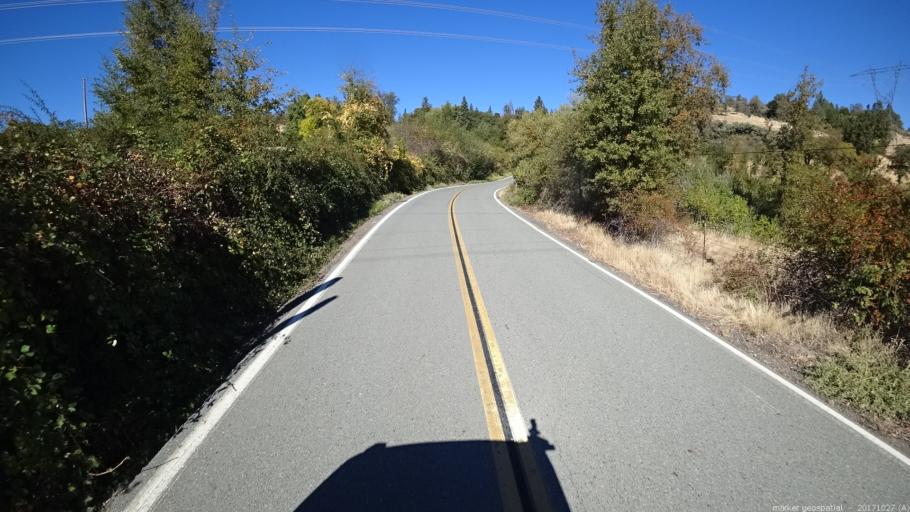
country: US
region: California
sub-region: Shasta County
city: Bella Vista
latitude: 40.7514
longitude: -121.9956
